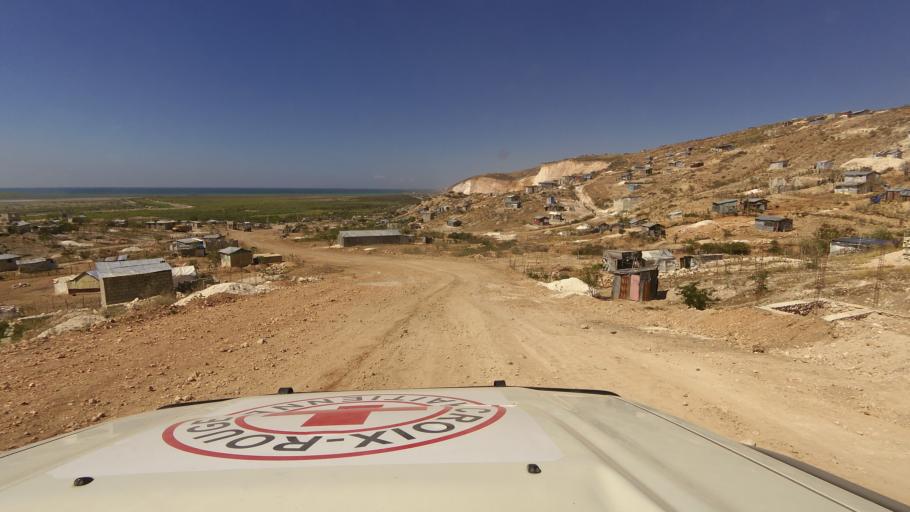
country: HT
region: Ouest
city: Croix des Bouquets
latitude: 18.6667
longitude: -72.2948
